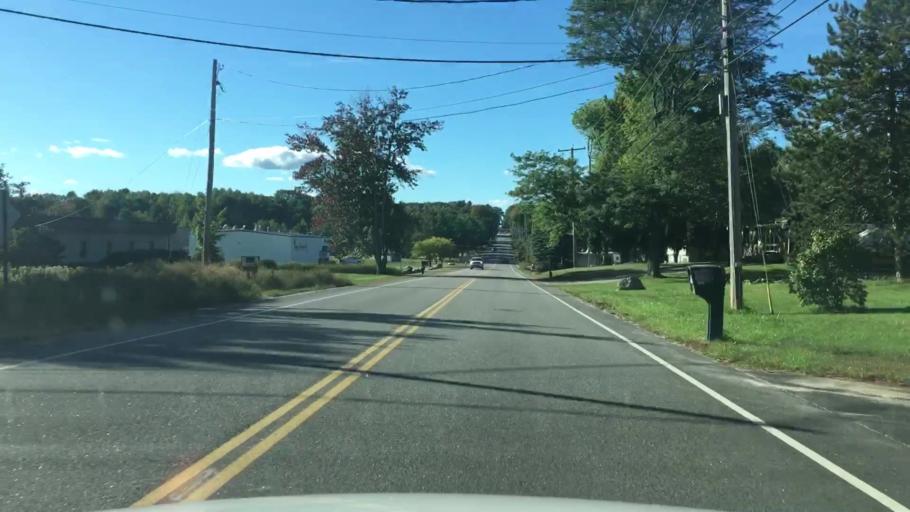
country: US
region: Maine
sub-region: Androscoggin County
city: Lewiston
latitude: 44.0790
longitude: -70.1643
